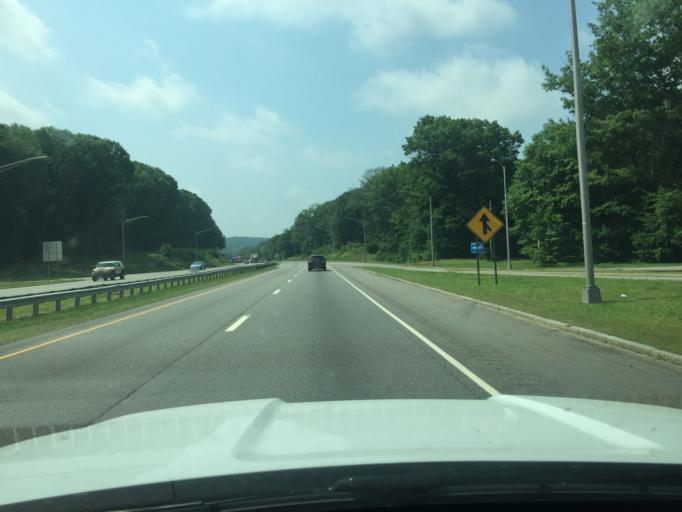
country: US
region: Connecticut
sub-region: New London County
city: Oxoboxo River
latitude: 41.4729
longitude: -72.1167
